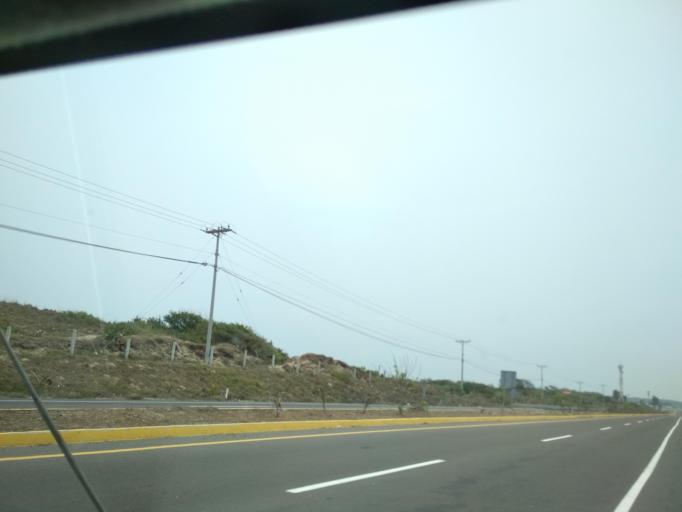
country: MX
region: Veracruz
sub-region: Alvarado
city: Playa de la Libertad
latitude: 19.0556
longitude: -96.0499
